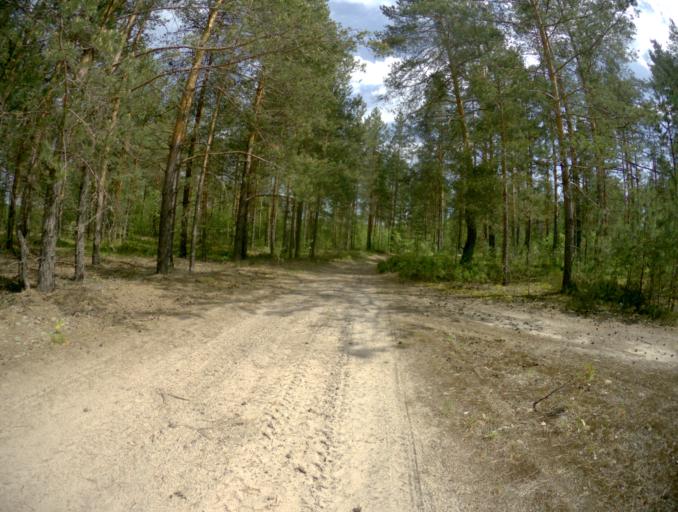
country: RU
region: Vladimir
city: Ivanishchi
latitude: 55.6822
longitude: 40.3994
